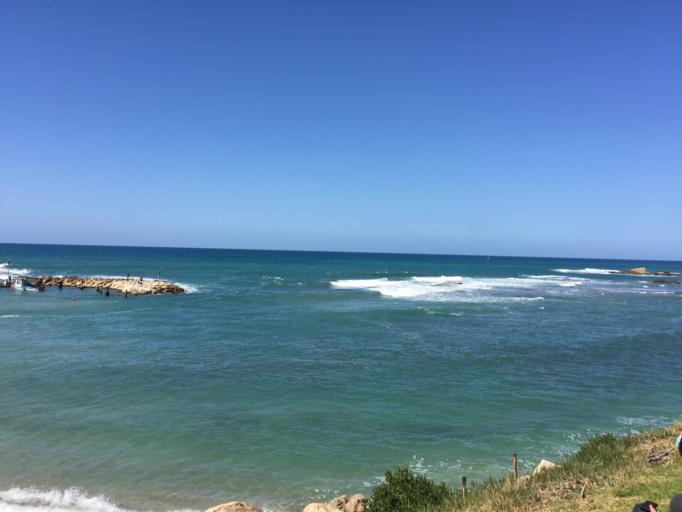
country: IL
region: Haifa
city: Qesarya
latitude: 32.4938
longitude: 34.8900
